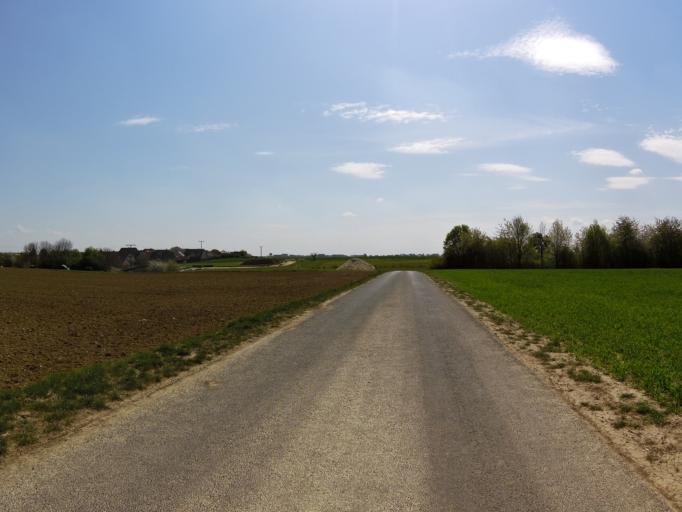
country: DE
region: Bavaria
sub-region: Regierungsbezirk Unterfranken
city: Giebelstadt
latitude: 49.6740
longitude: 9.9516
